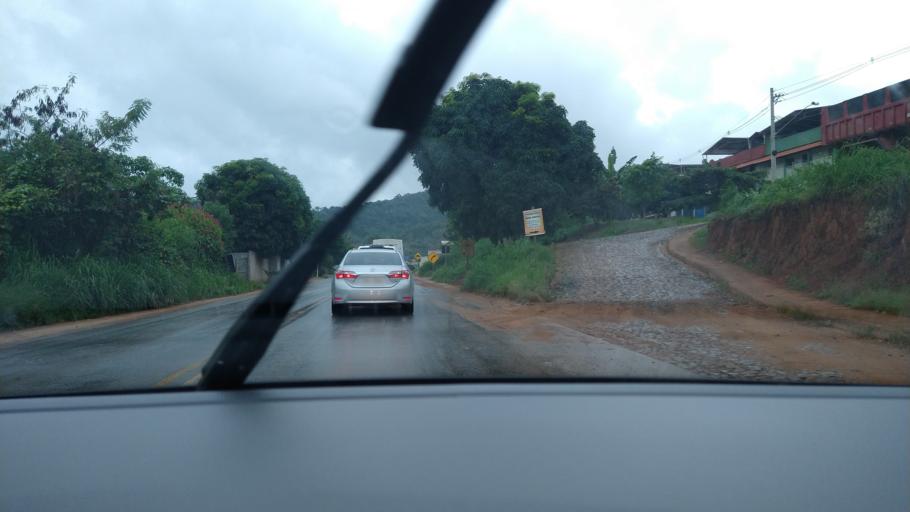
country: BR
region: Minas Gerais
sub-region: Vicosa
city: Vicosa
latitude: -20.6367
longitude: -42.8687
